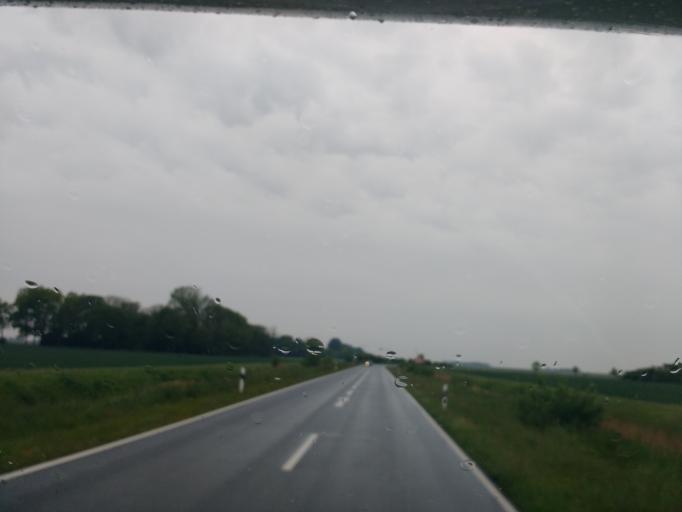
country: DE
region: Lower Saxony
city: Werdum
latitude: 53.6860
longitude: 7.7942
